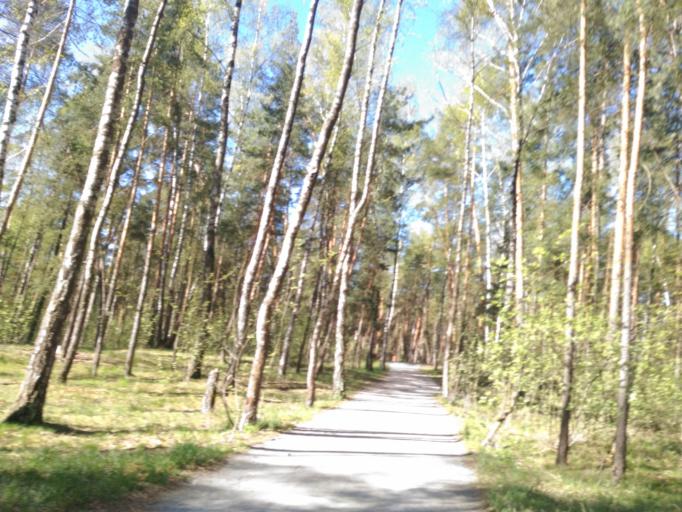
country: RU
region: Moscow
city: Shchukino
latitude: 55.7799
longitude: 37.4176
